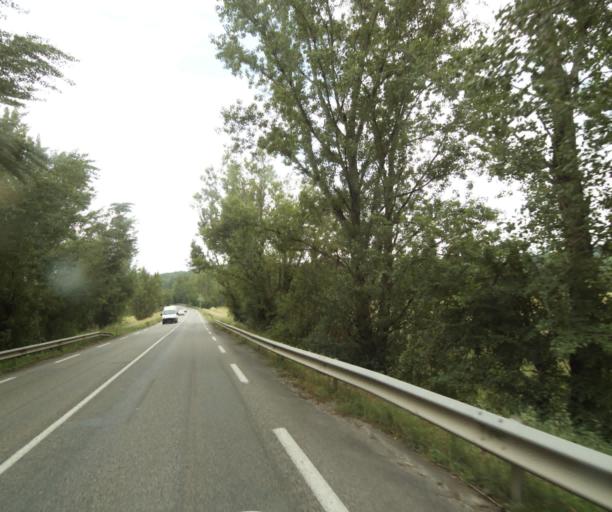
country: FR
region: Midi-Pyrenees
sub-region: Departement du Tarn-et-Garonne
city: Saint-Nauphary
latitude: 43.9850
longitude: 1.3933
